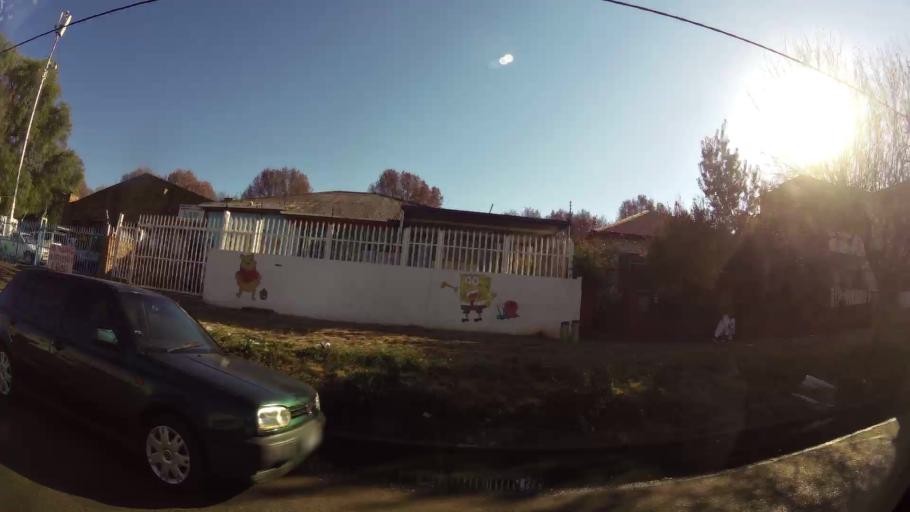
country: ZA
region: Gauteng
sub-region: City of Johannesburg Metropolitan Municipality
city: Johannesburg
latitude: -26.2021
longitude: 28.1084
